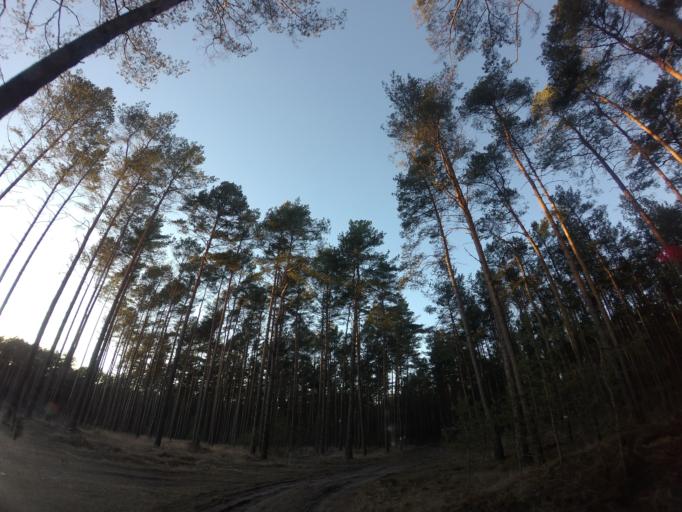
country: PL
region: West Pomeranian Voivodeship
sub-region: Powiat choszczenski
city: Drawno
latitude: 53.1186
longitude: 15.7522
